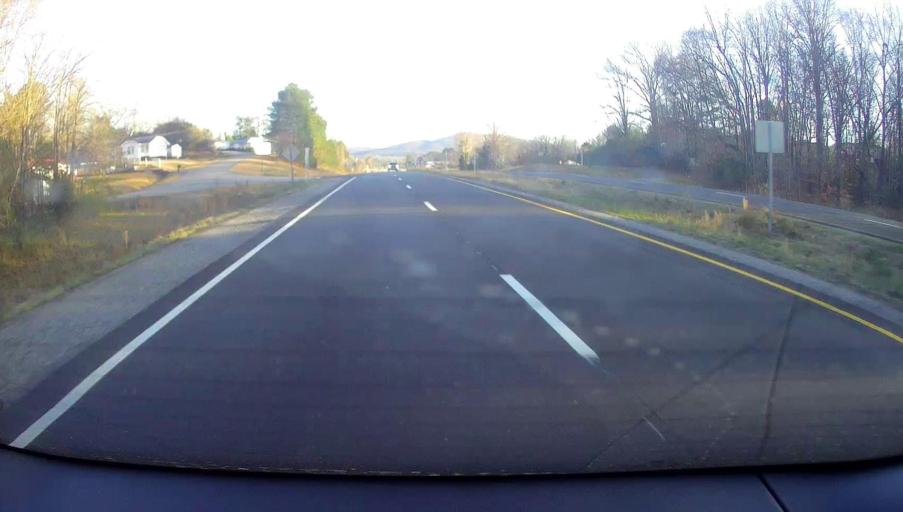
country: US
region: Alabama
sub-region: Calhoun County
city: Saks
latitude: 33.7089
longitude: -85.8378
